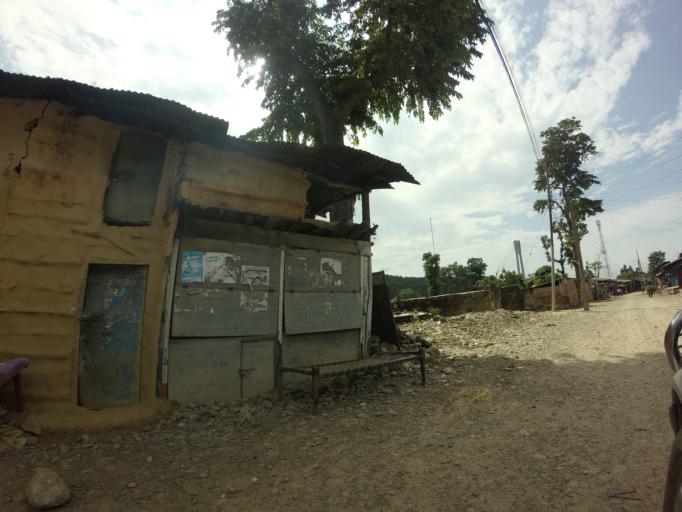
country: NP
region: Far Western
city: Tikapur
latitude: 28.6465
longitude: 81.2844
